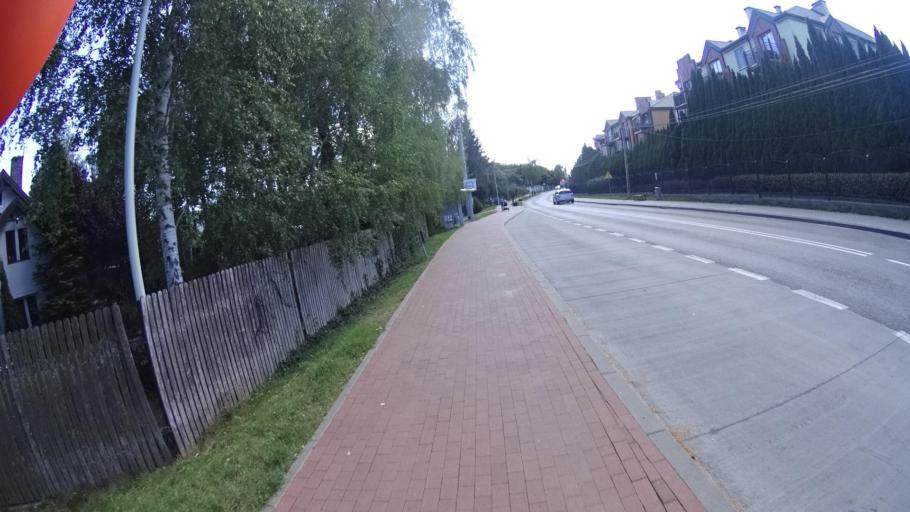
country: PL
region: Masovian Voivodeship
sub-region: Powiat piaseczynski
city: Jozefoslaw
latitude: 52.0963
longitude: 21.0531
